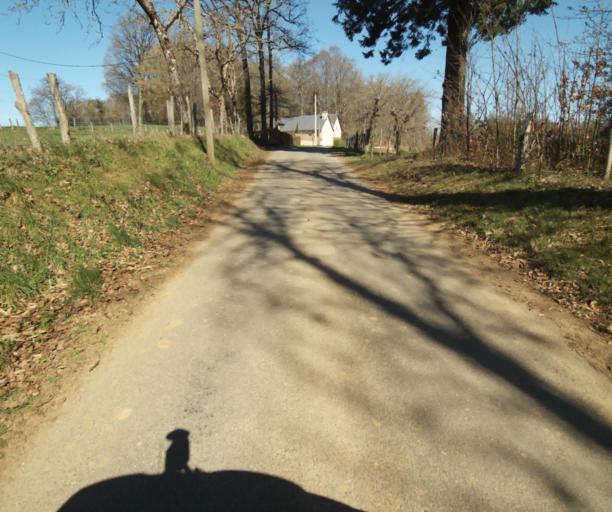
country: FR
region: Limousin
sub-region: Departement de la Correze
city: Seilhac
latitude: 45.3512
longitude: 1.7289
